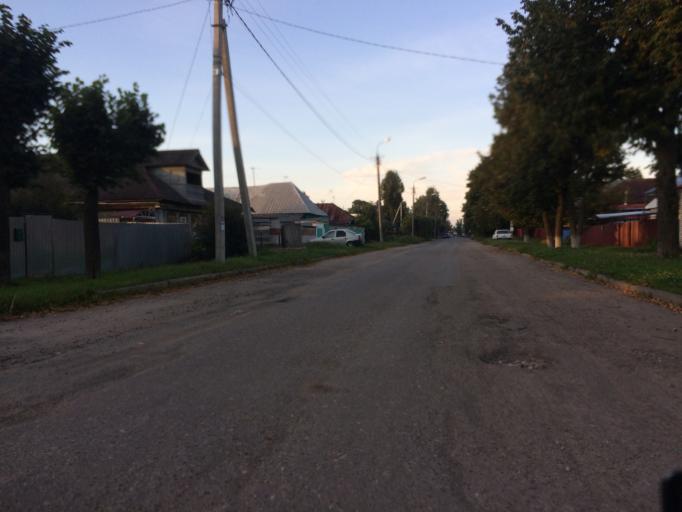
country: RU
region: Mariy-El
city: Yoshkar-Ola
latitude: 56.6524
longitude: 47.9040
